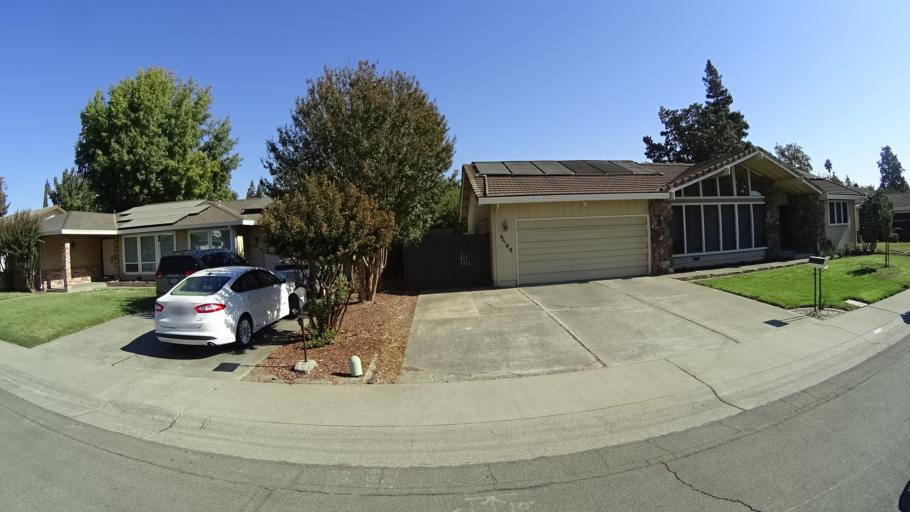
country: US
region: California
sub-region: Yolo County
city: West Sacramento
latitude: 38.5052
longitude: -121.5423
